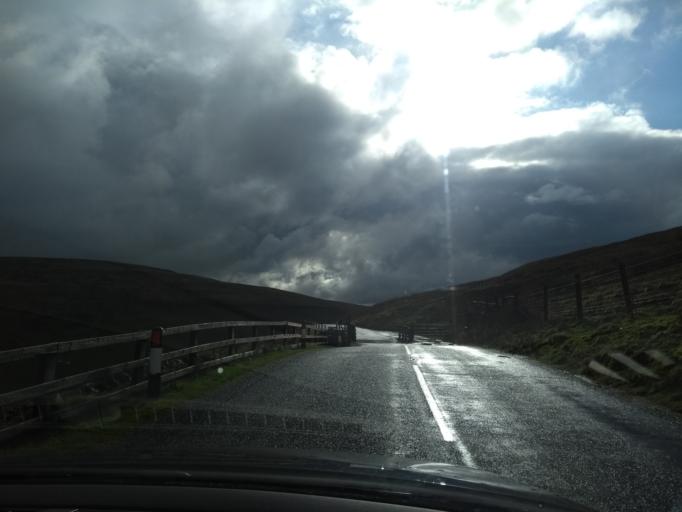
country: GB
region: England
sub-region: Cumbria
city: Kirkby Stephen
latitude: 54.3668
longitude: -2.1888
